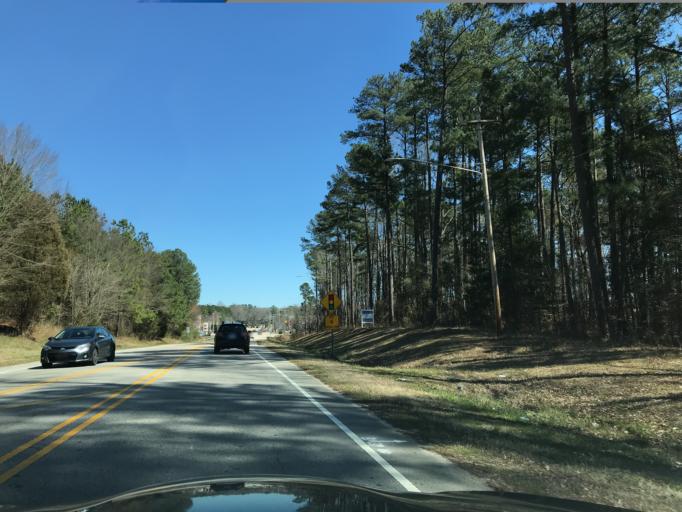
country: US
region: North Carolina
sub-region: Wake County
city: Wake Forest
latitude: 35.9768
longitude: -78.5463
